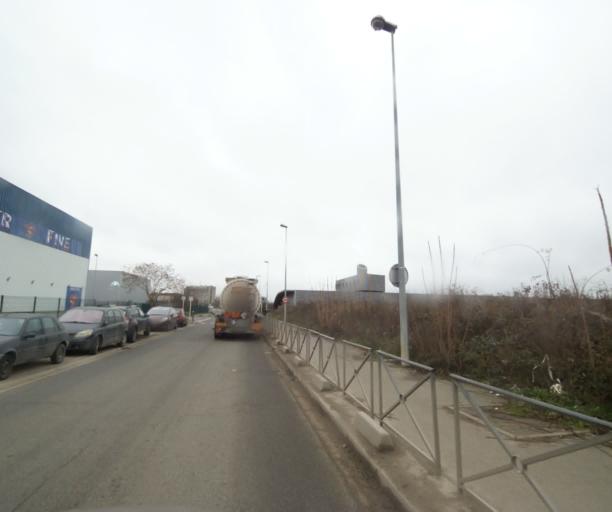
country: FR
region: Ile-de-France
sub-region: Departement du Val-de-Marne
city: Ablon-sur-Seine
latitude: 48.7305
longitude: 2.4336
